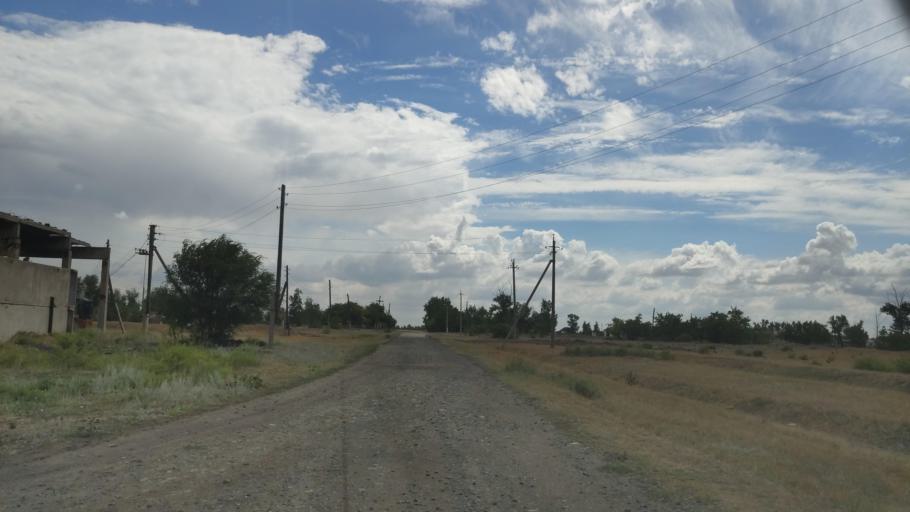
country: KZ
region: Pavlodar
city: Pavlodar
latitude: 52.6506
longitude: 77.0220
